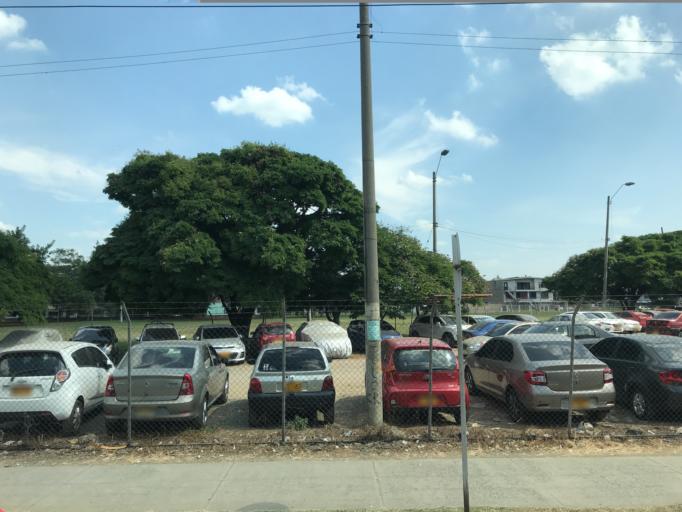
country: CO
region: Valle del Cauca
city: Cali
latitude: 3.4920
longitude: -76.4963
